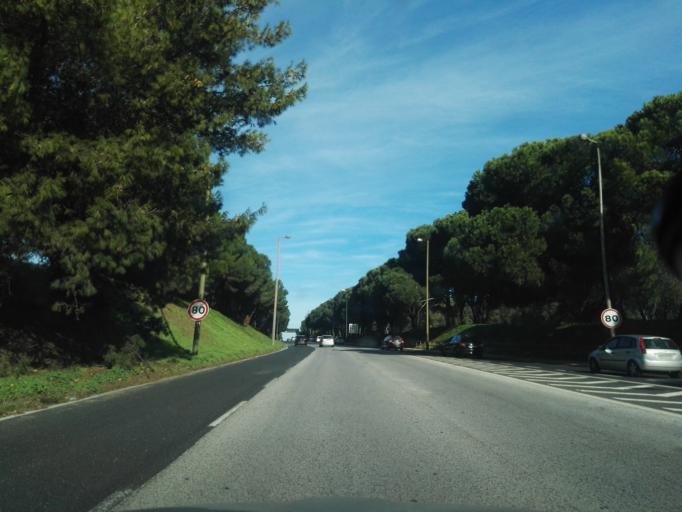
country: PT
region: Lisbon
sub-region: Loures
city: Moscavide
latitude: 38.7726
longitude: -9.1236
